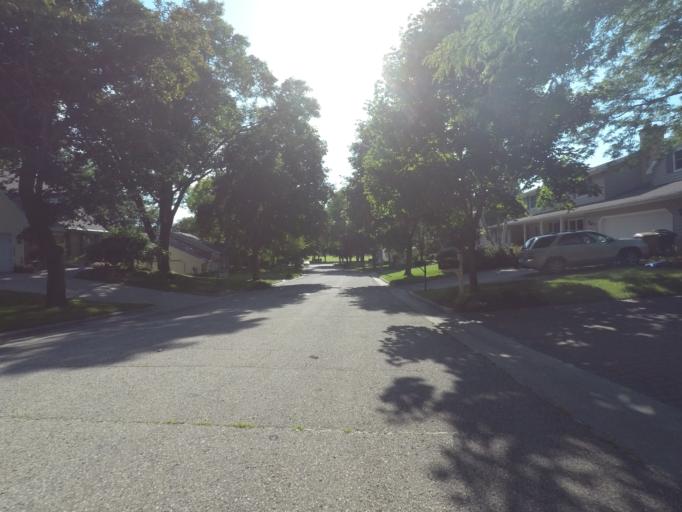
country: US
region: Wisconsin
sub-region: Dane County
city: Middleton
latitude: 43.0684
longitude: -89.5069
